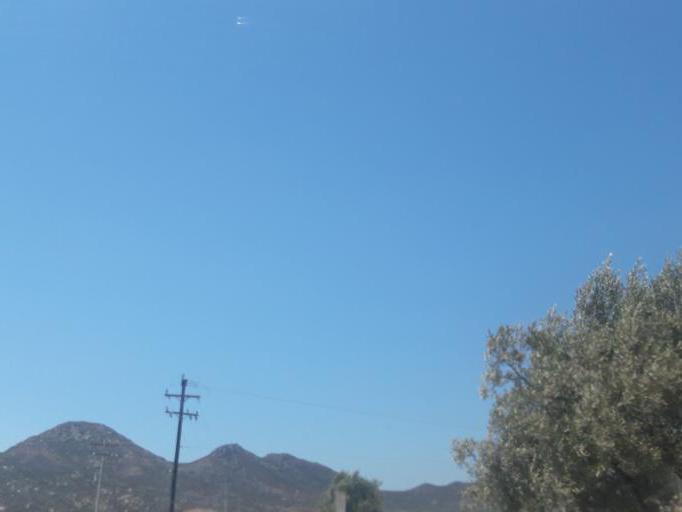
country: MX
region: Baja California
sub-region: Ensenada
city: Rancho Verde
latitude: 32.0921
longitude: -116.6311
